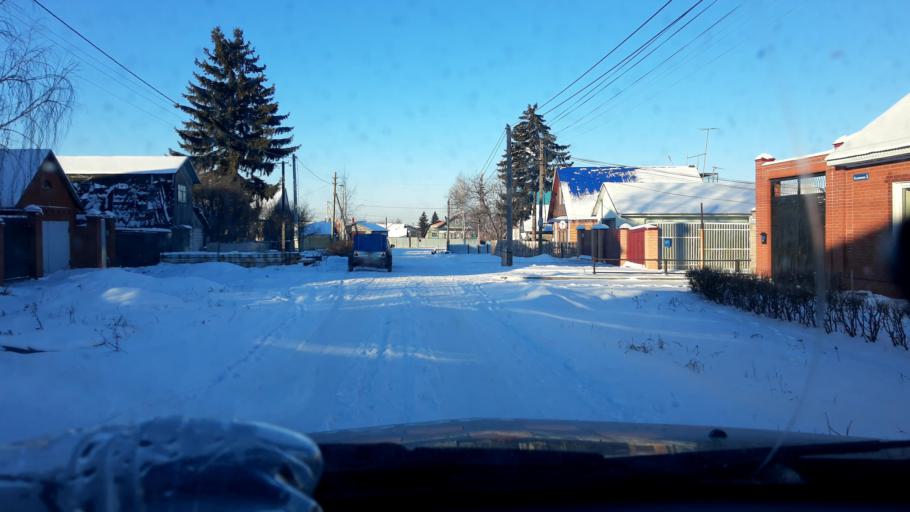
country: RU
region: Bashkortostan
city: Ufa
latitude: 54.6130
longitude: 55.9425
